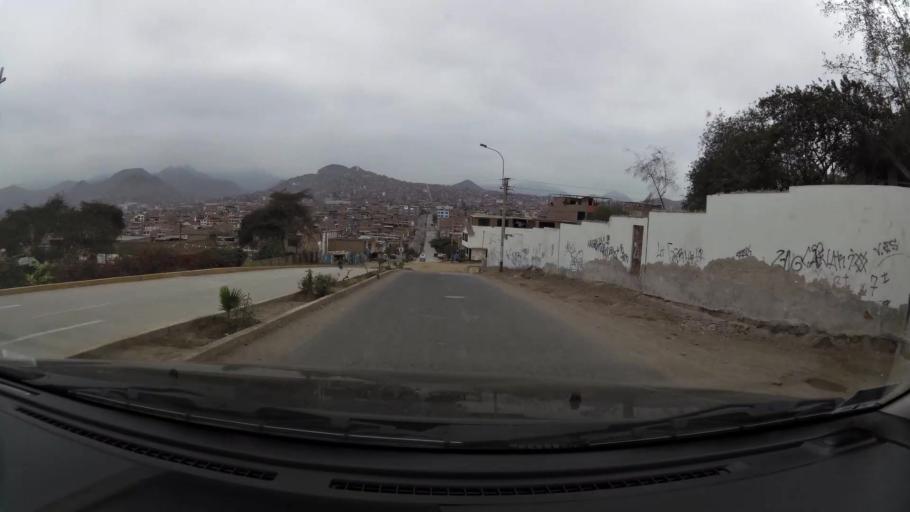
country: PE
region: Lima
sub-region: Lima
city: Surco
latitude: -12.1960
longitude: -76.9479
